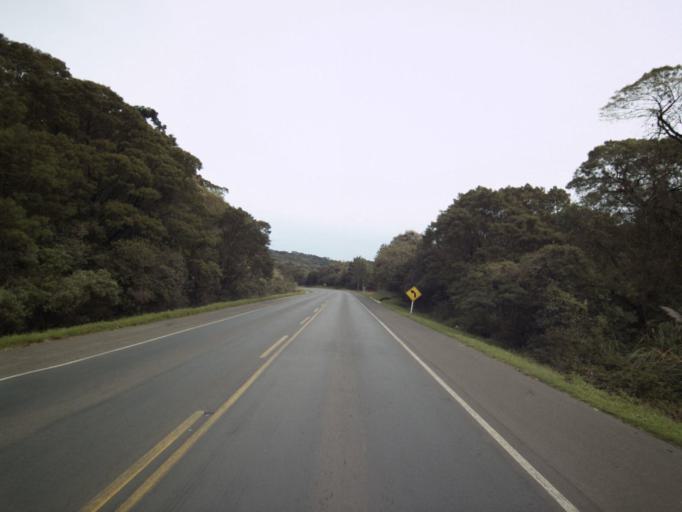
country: BR
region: Parana
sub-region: Palmas
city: Palmas
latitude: -26.6396
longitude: -51.5121
